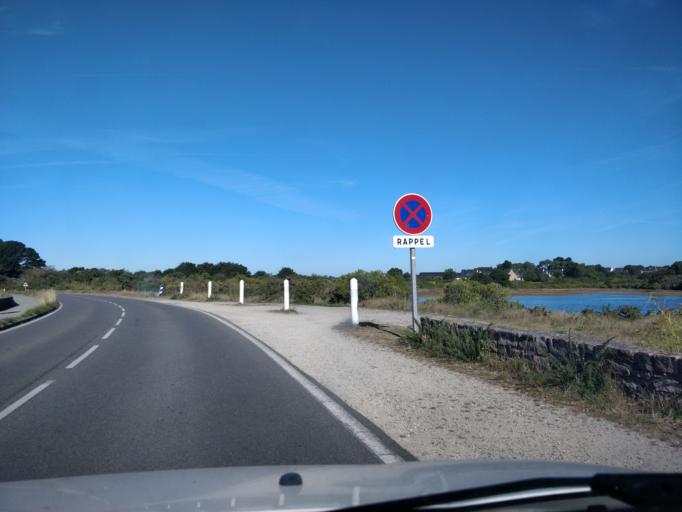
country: FR
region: Brittany
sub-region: Departement du Morbihan
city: La Trinite-sur-Mer
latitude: 47.5794
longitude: -3.0409
